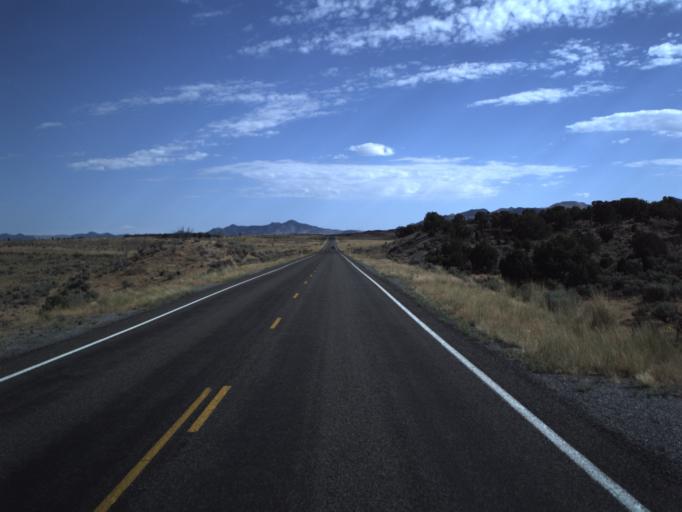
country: US
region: Utah
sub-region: Juab County
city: Mona
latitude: 39.7395
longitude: -112.1893
